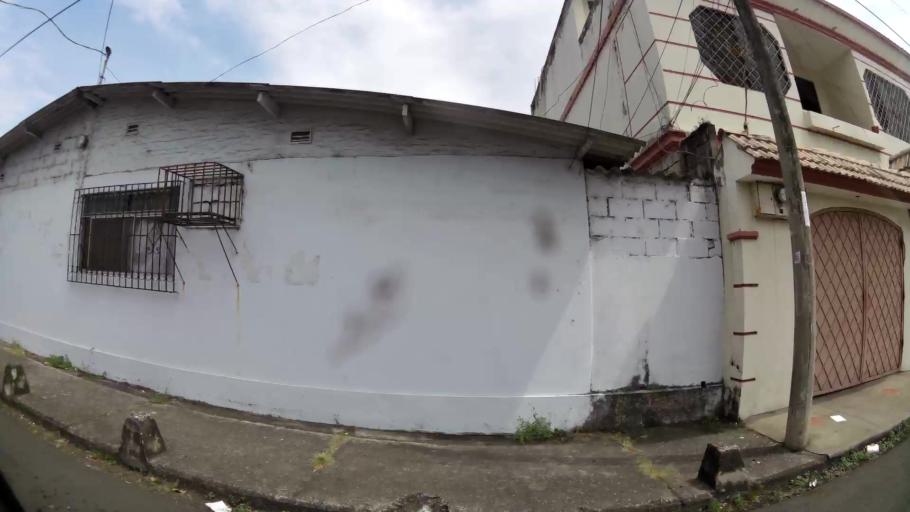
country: EC
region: Guayas
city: Eloy Alfaro
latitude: -2.1410
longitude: -79.8991
